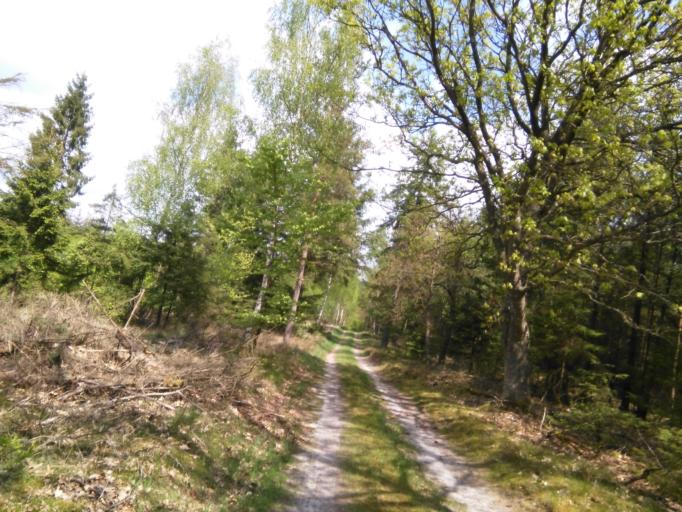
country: DK
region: Central Jutland
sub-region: Silkeborg Kommune
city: Svejbaek
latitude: 56.0585
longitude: 9.6377
